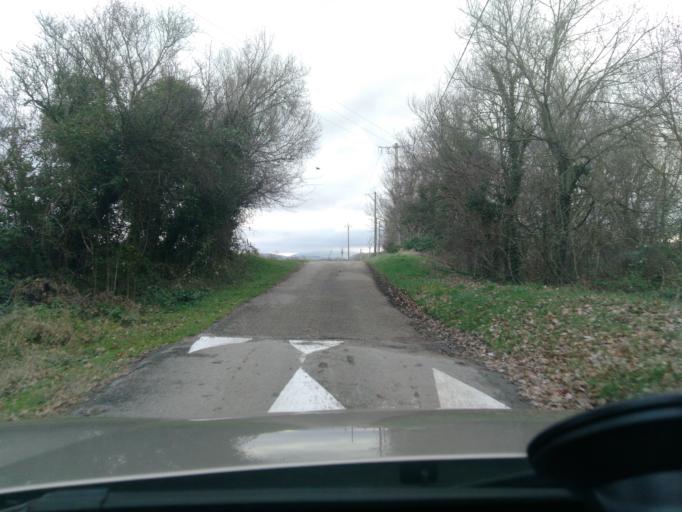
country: FR
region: Rhone-Alpes
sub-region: Departement de la Drome
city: Montboucher-sur-Jabron
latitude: 44.5493
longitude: 4.8607
